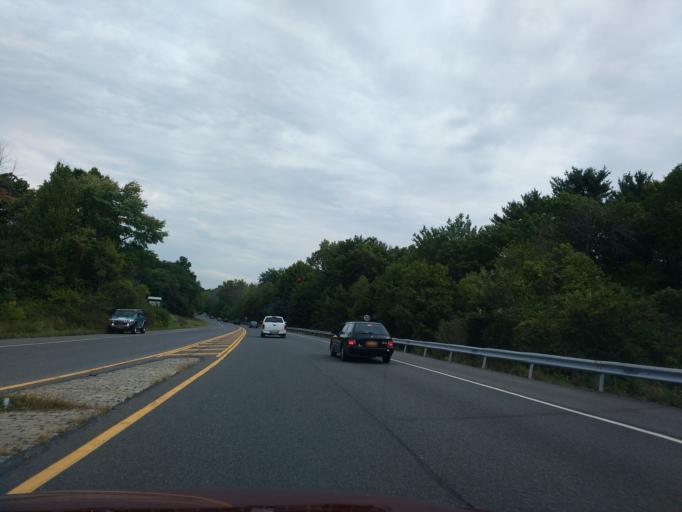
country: US
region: New York
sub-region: Ulster County
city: Lincoln Park
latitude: 41.9453
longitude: -73.9818
